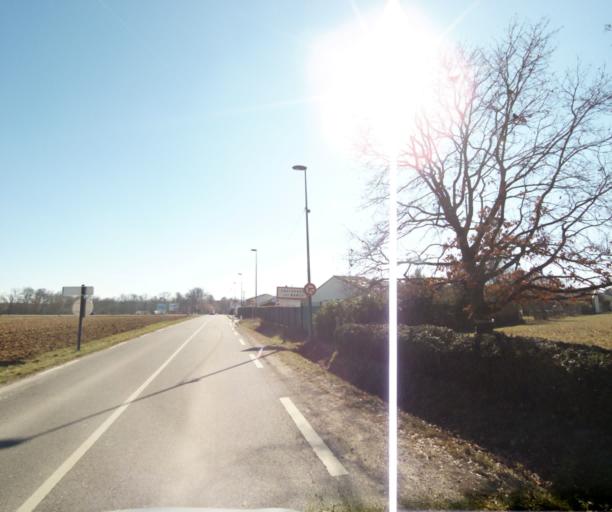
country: FR
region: Lorraine
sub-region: Departement de Meurthe-et-Moselle
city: Saulxures-les-Nancy
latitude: 48.6943
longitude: 6.2503
